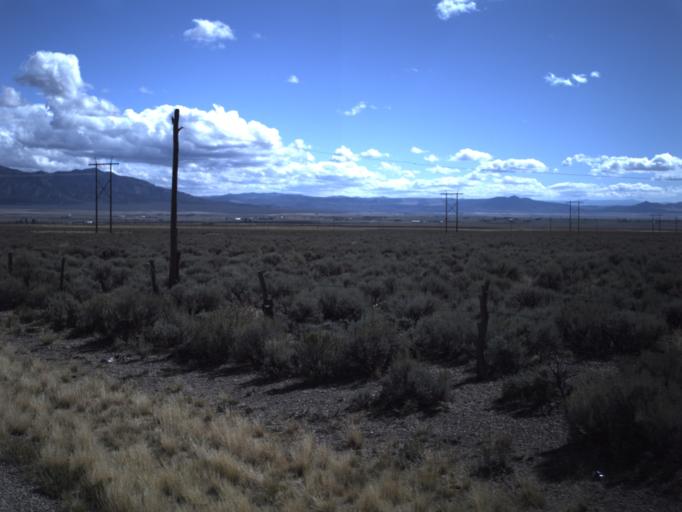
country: US
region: Utah
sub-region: Beaver County
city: Milford
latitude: 38.4102
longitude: -113.0632
